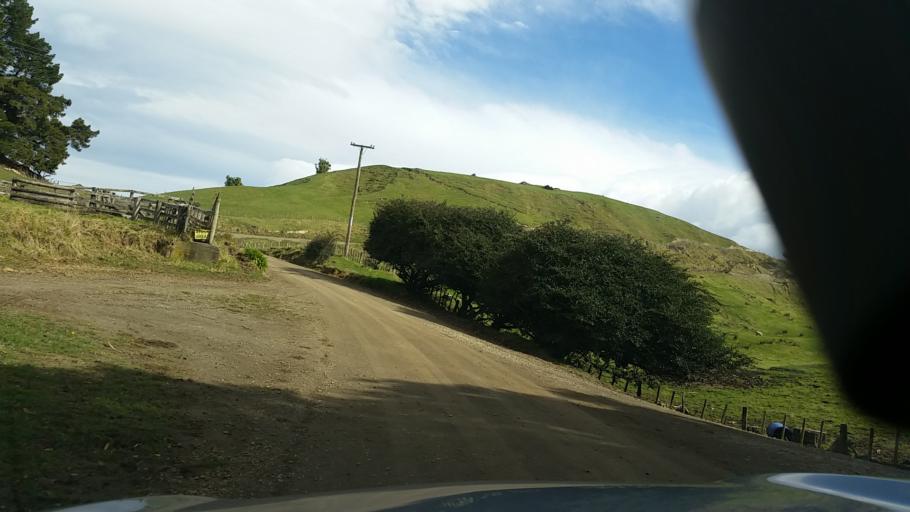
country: NZ
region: Hawke's Bay
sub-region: Napier City
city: Napier
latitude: -39.2113
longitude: 176.9679
